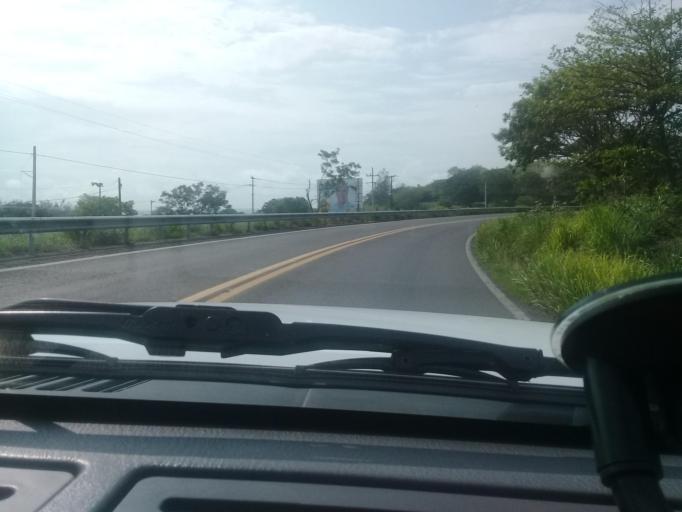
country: MX
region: Veracruz
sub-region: Paso de Ovejas
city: Tolome
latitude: 19.2653
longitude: -96.3747
